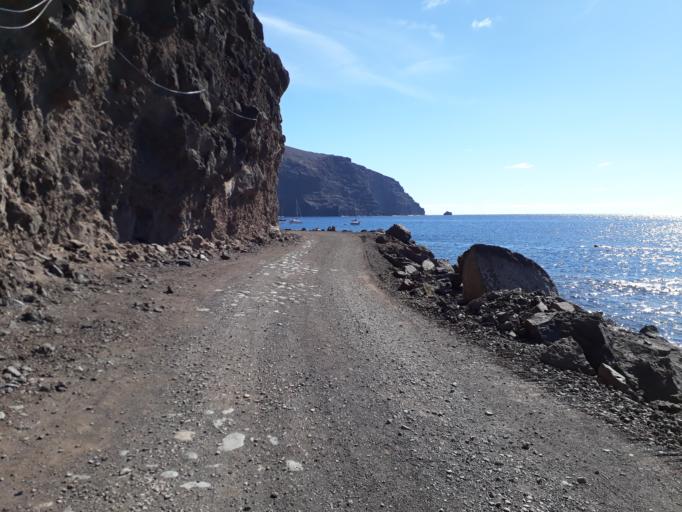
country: ES
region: Canary Islands
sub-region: Provincia de Santa Cruz de Tenerife
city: Alajero
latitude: 28.0811
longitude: -17.3297
